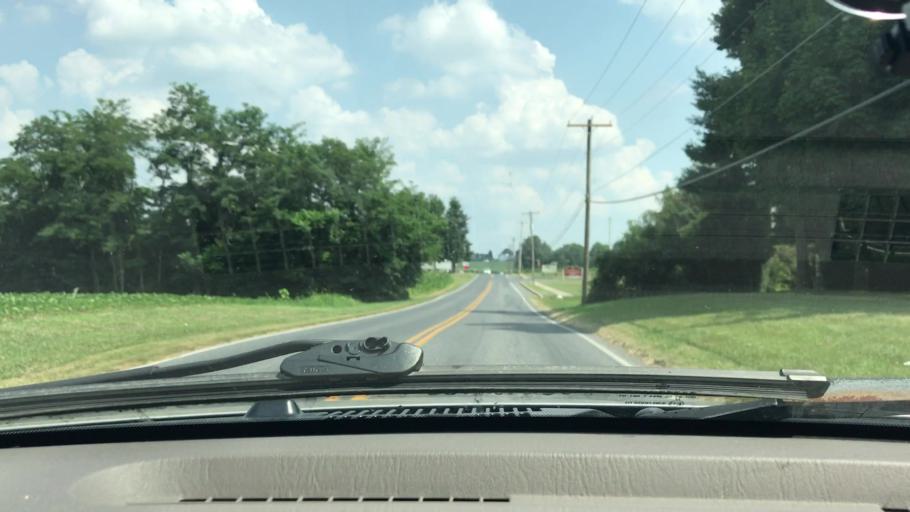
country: US
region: Pennsylvania
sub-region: Lancaster County
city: Elizabethtown
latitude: 40.1642
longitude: -76.5765
